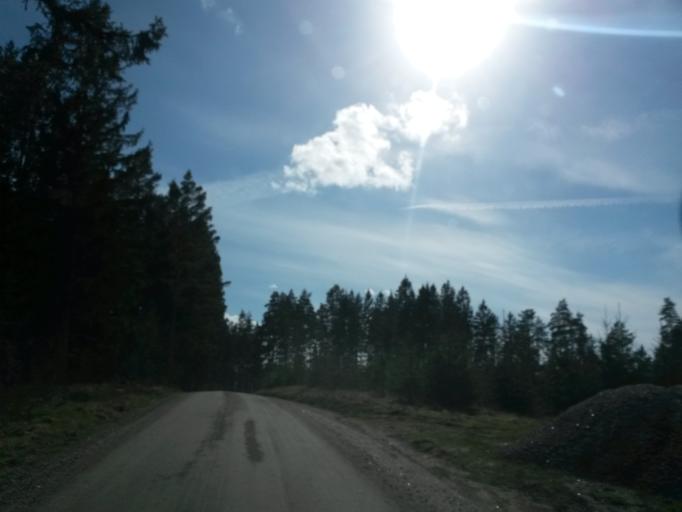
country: SE
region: Vaestra Goetaland
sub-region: Vargarda Kommun
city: Jonstorp
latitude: 57.9808
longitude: 12.7525
